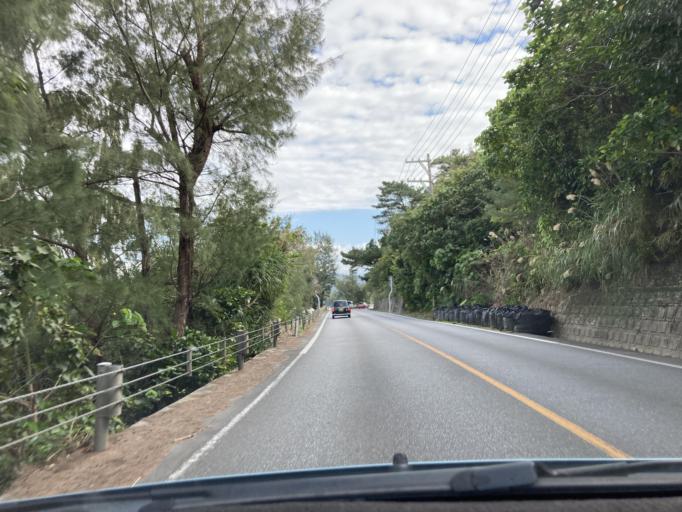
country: JP
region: Okinawa
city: Nago
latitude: 26.6387
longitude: 128.0027
